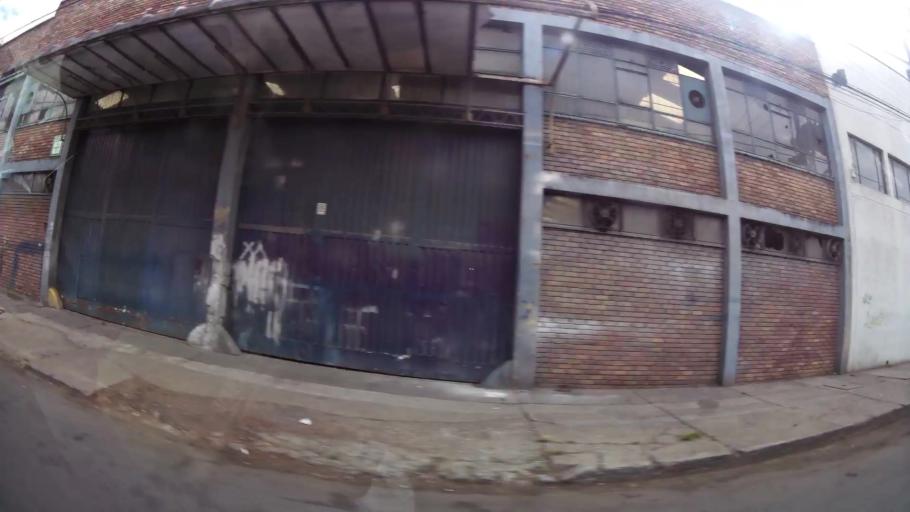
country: CO
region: Bogota D.C.
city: Bogota
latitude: 4.6186
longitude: -74.1016
